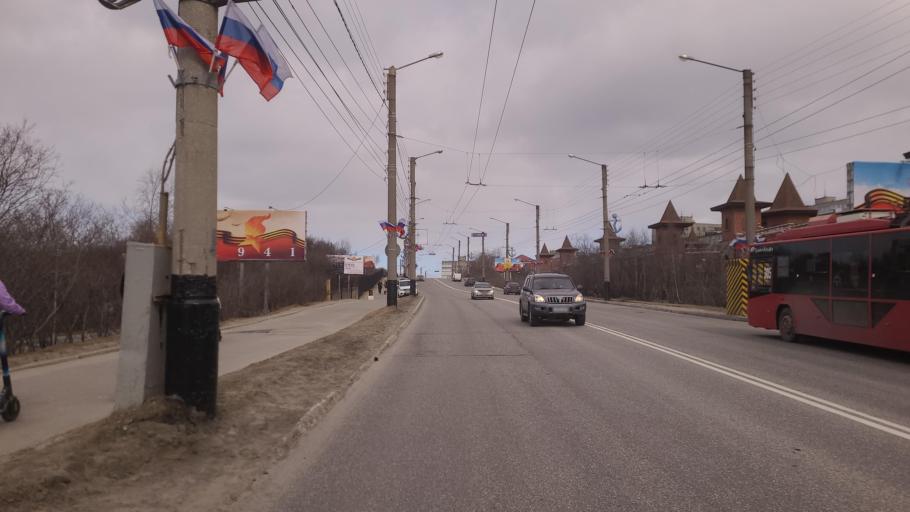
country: RU
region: Murmansk
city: Murmansk
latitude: 68.9883
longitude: 33.0940
